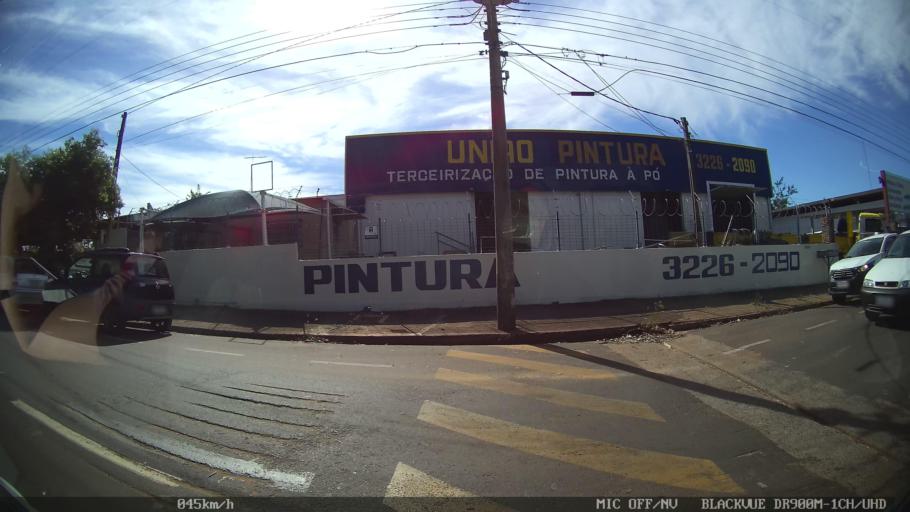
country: BR
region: Sao Paulo
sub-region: Sao Jose Do Rio Preto
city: Sao Jose do Rio Preto
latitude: -20.8502
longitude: -49.3856
